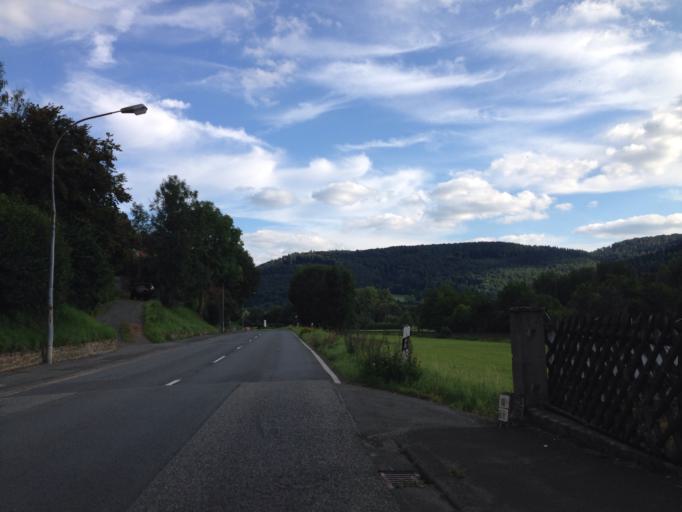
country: DE
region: Hesse
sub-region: Regierungsbezirk Giessen
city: Biedenkopf
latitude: 50.9201
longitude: 8.5073
